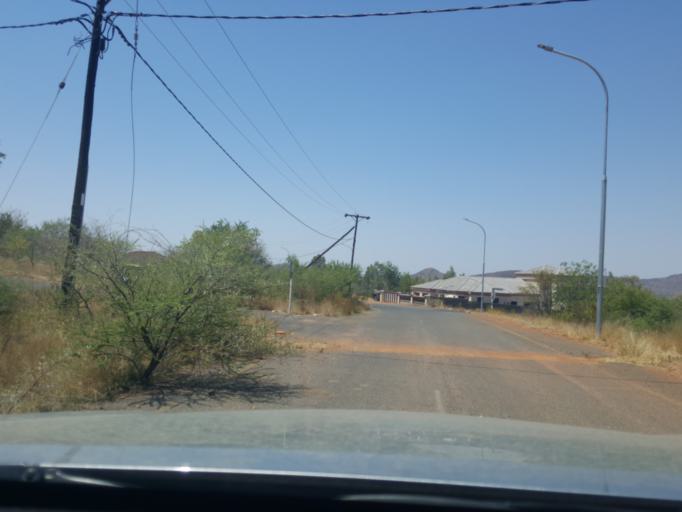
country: BW
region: South East
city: Lobatse
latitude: -25.1882
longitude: 25.6775
